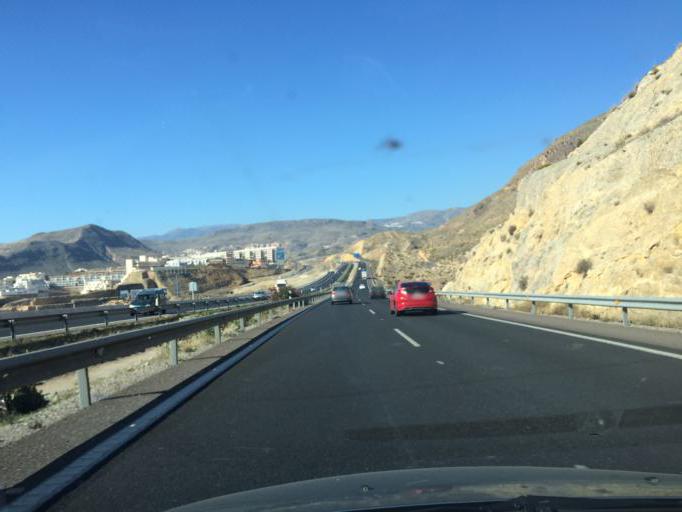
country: ES
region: Andalusia
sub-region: Provincia de Almeria
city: Aguadulce
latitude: 36.8235
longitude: -2.5765
